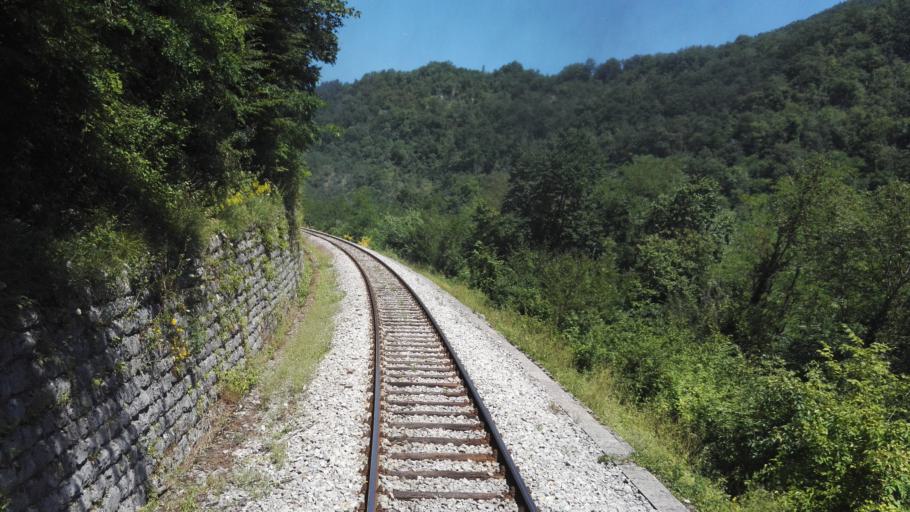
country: SI
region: Kanal
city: Deskle
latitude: 46.0235
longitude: 13.6052
